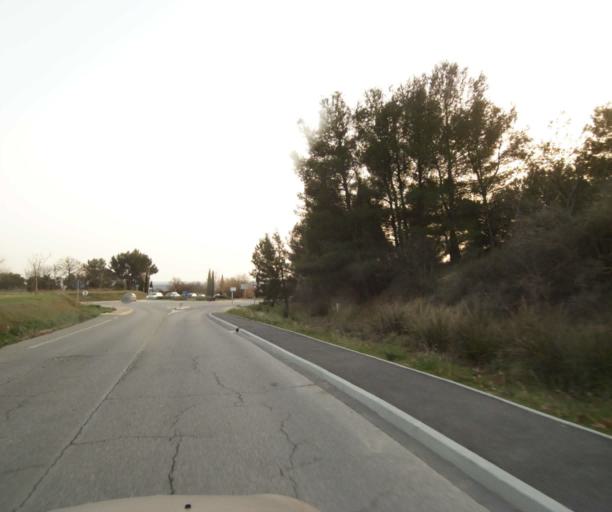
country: FR
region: Provence-Alpes-Cote d'Azur
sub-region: Departement des Bouches-du-Rhone
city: Eguilles
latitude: 43.5615
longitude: 5.3531
